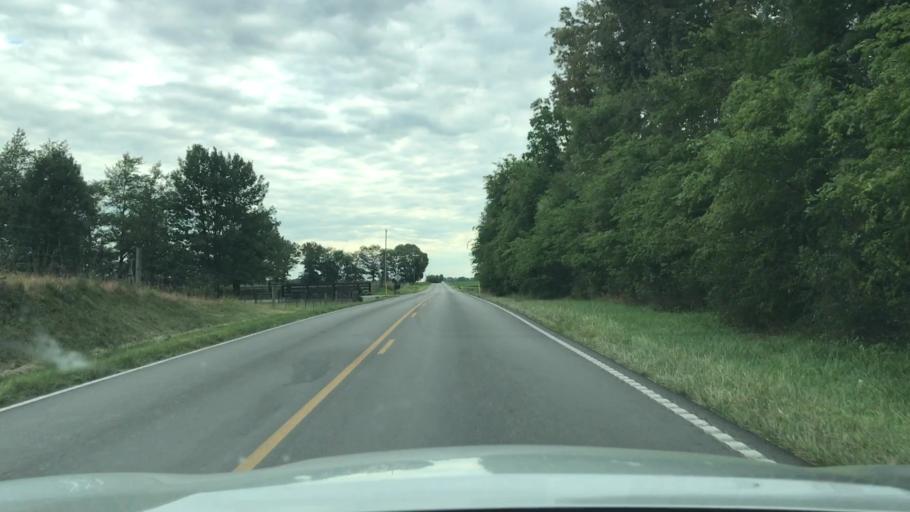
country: US
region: Kentucky
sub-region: Todd County
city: Elkton
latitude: 36.7364
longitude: -87.1865
